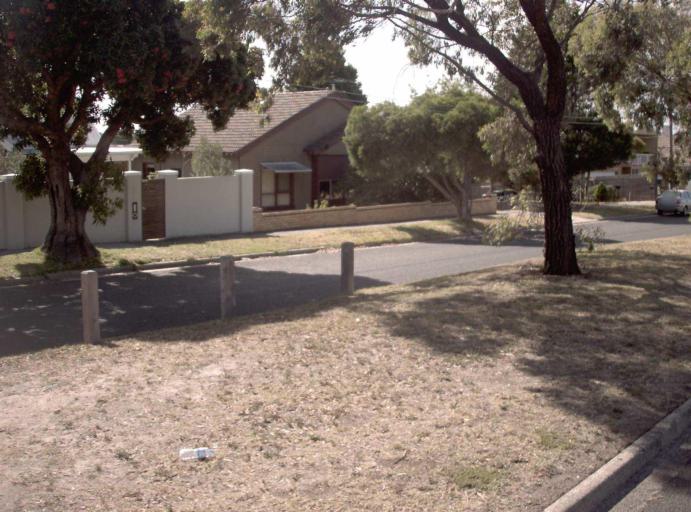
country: AU
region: Victoria
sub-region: Kingston
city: Mordialloc
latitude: -38.0036
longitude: 145.0848
